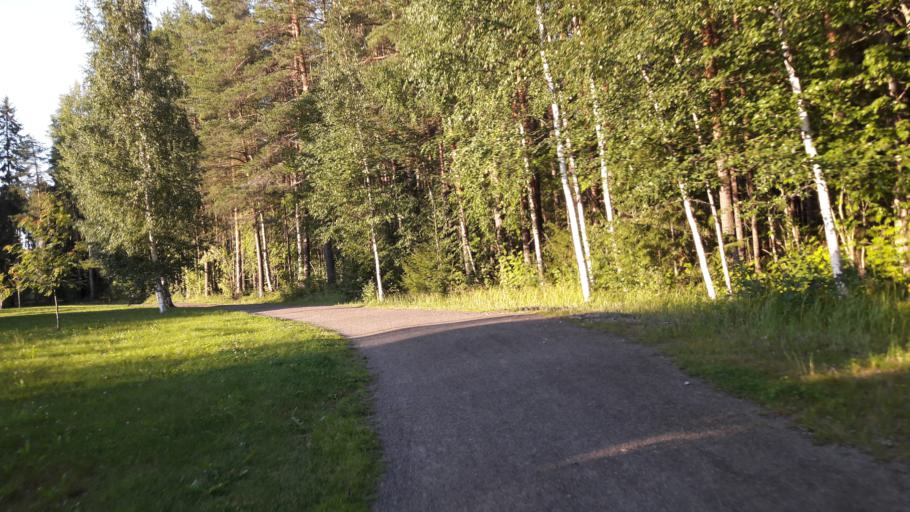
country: FI
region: North Karelia
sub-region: Joensuu
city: Joensuu
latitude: 62.6139
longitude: 29.7160
